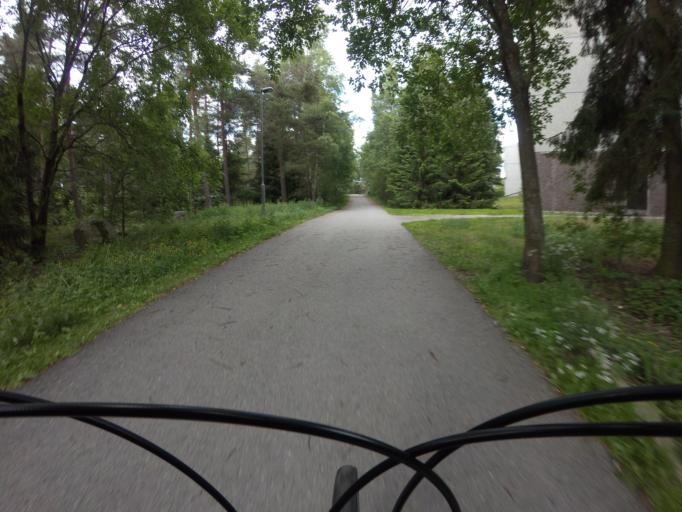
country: FI
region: Varsinais-Suomi
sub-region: Turku
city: Vahto
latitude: 60.5400
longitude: 22.3485
